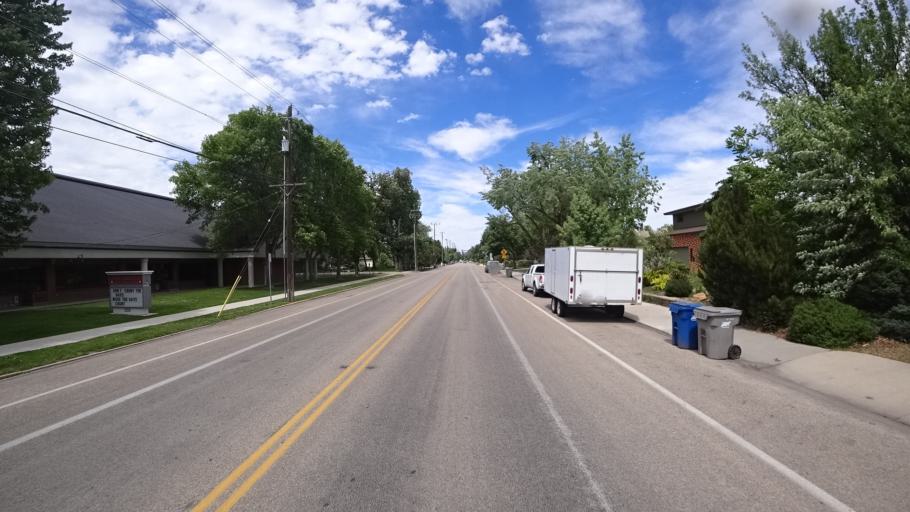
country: US
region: Idaho
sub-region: Ada County
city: Boise
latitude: 43.6033
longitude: -116.1738
